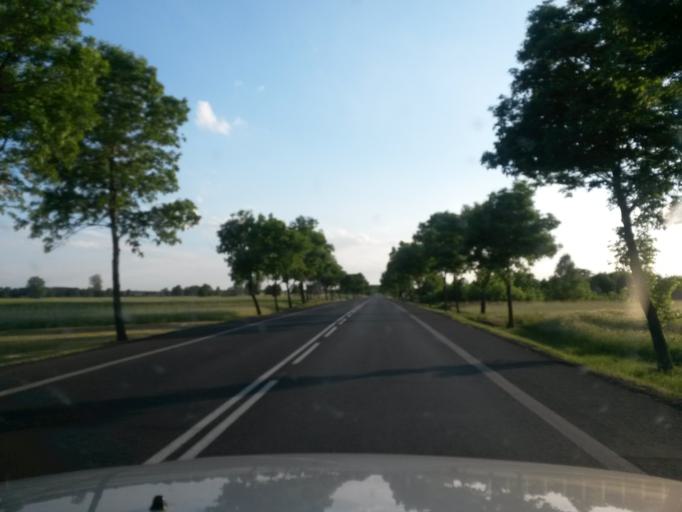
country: PL
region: Lodz Voivodeship
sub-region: Powiat wielunski
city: Osjakow
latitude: 51.2815
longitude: 18.7757
